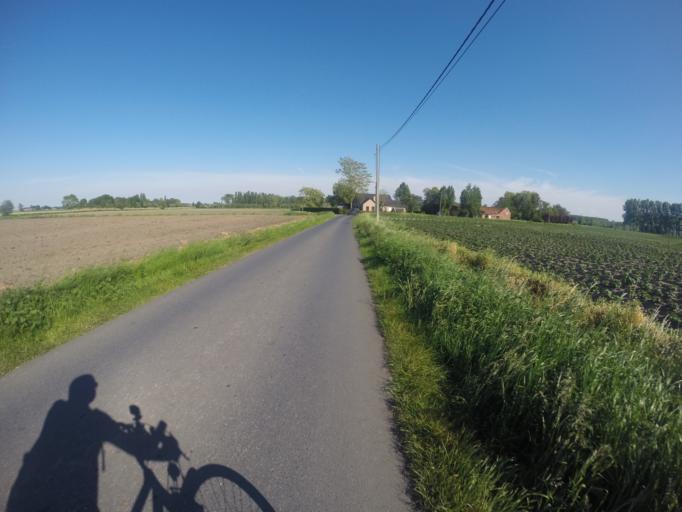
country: BE
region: Flanders
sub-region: Provincie Oost-Vlaanderen
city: Aalter
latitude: 51.0711
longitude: 3.4224
